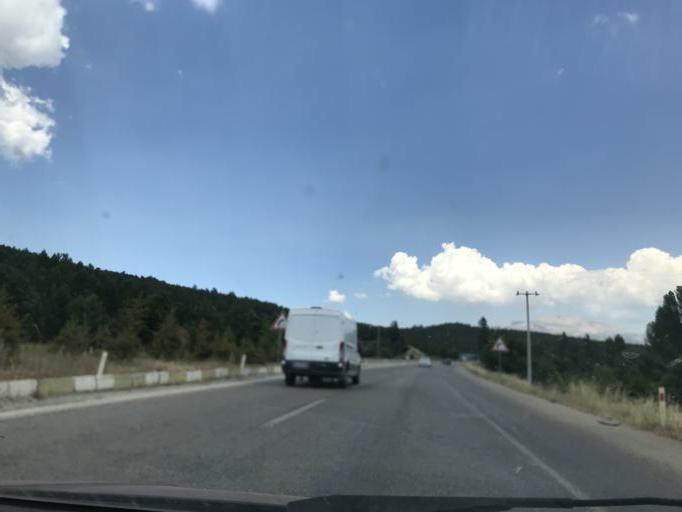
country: TR
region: Denizli
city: Tavas
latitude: 37.6114
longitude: 29.1393
